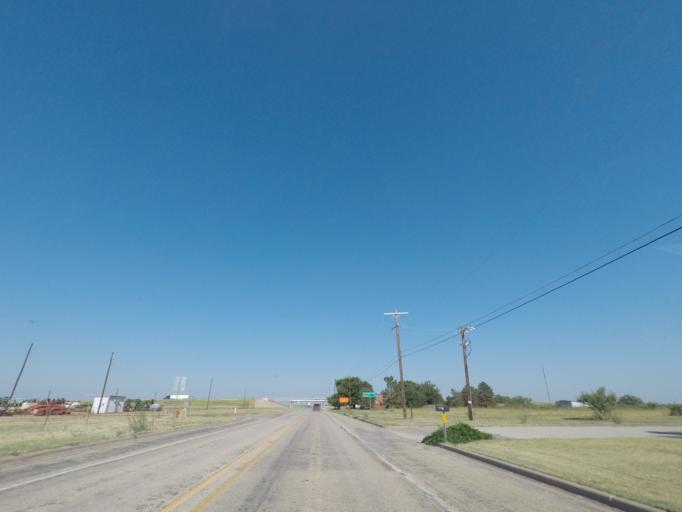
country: US
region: Texas
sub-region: Baylor County
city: Seymour
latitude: 33.5959
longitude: -99.2451
